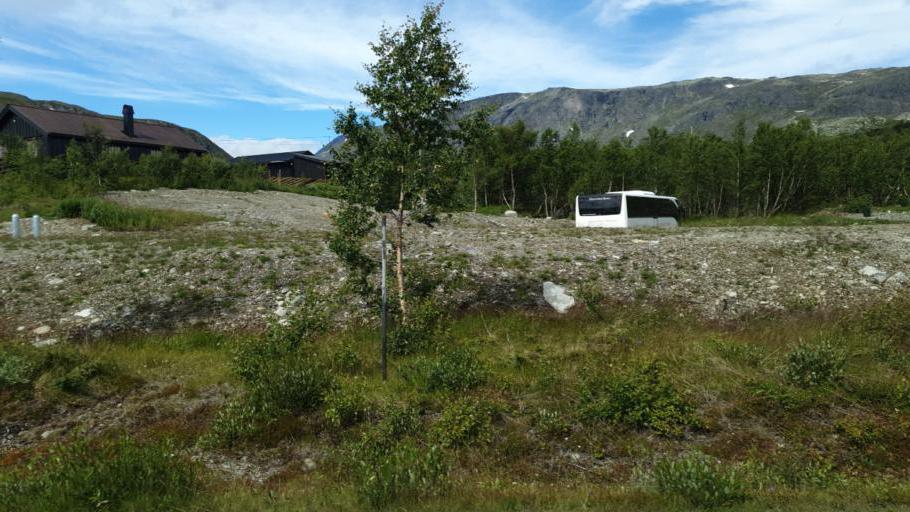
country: NO
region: Oppland
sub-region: Oystre Slidre
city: Heggenes
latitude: 61.4859
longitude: 8.8324
